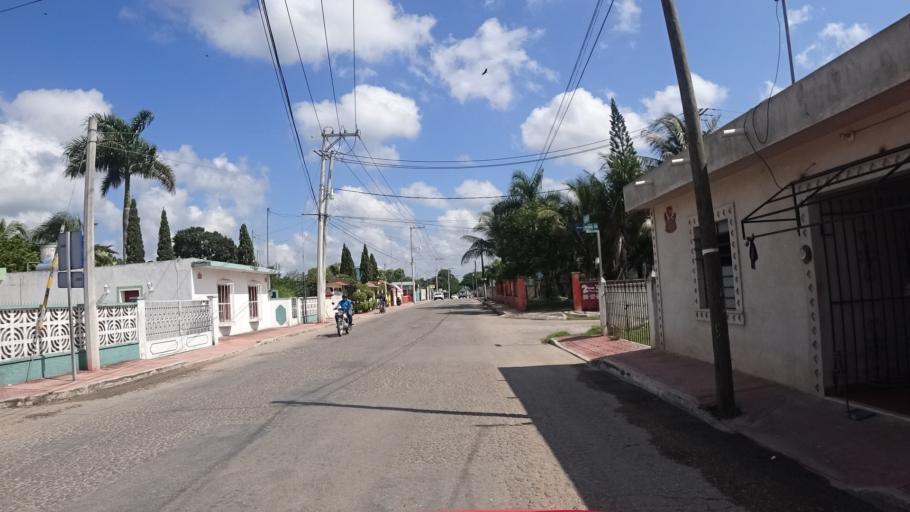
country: MX
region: Yucatan
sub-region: Tizimin
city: Tizimin
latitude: 21.1329
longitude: -88.1539
